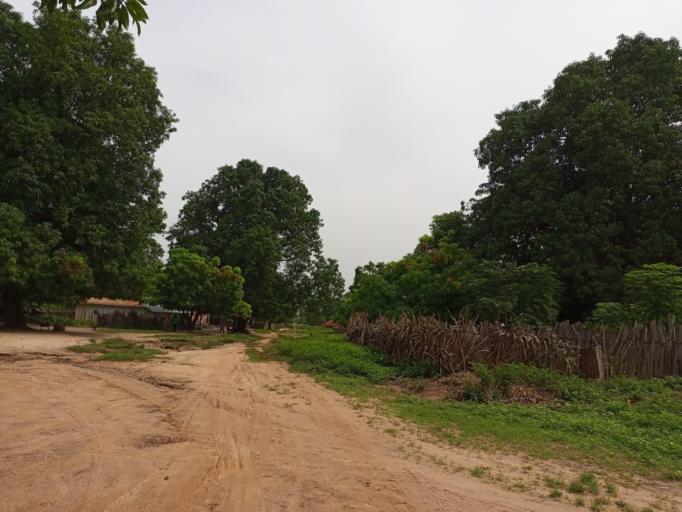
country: GW
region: Oio
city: Farim
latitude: 12.4596
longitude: -15.3046
